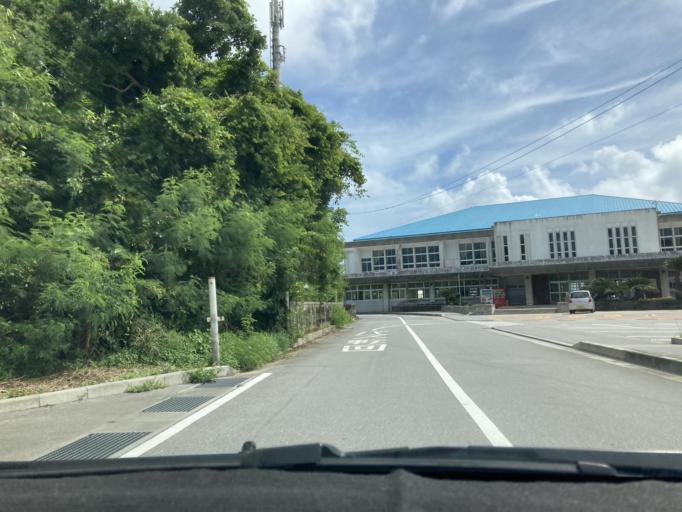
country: JP
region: Okinawa
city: Ginowan
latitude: 26.1682
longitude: 127.8282
